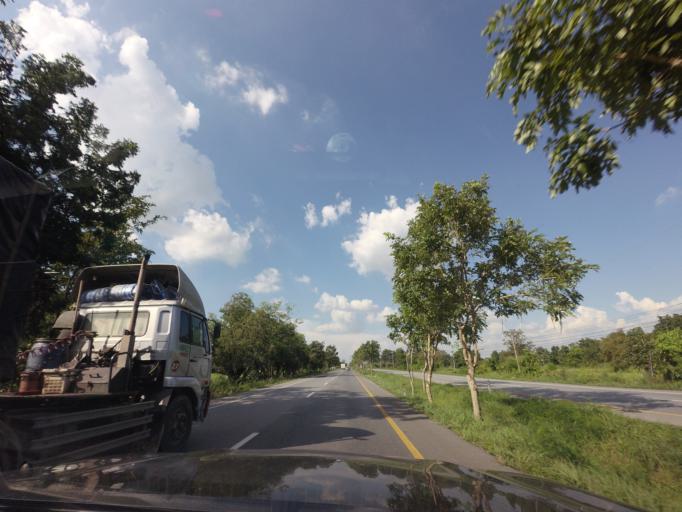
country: TH
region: Nakhon Ratchasima
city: Bua Lai
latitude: 15.7111
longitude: 102.5879
